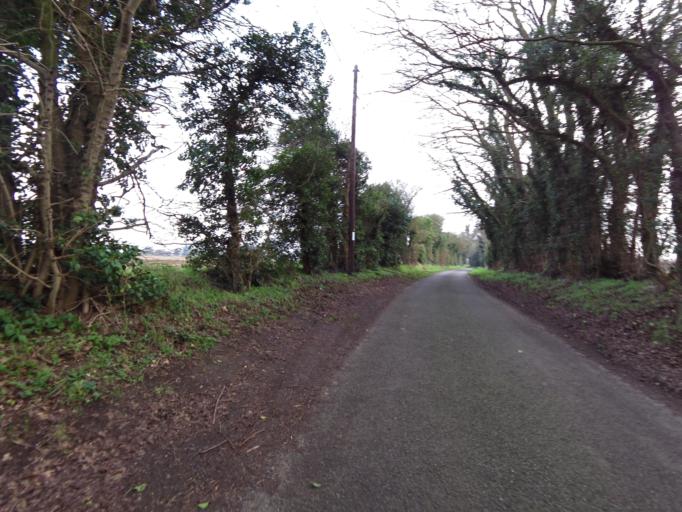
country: GB
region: England
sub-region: Suffolk
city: Woodbridge
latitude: 52.0613
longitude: 1.3129
